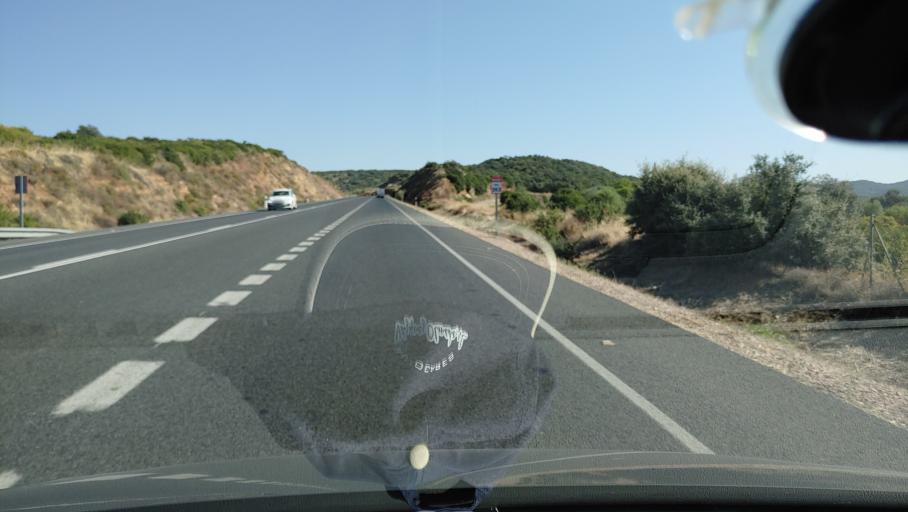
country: ES
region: Andalusia
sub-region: Province of Cordoba
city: Cordoba
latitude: 37.9347
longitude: -4.7644
